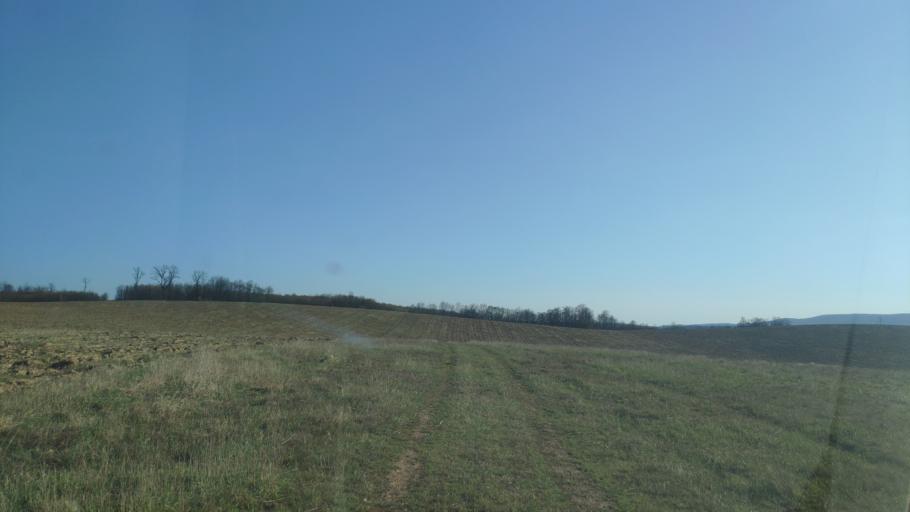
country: SK
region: Banskobystricky
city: Revuca
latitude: 48.5431
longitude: 20.2568
